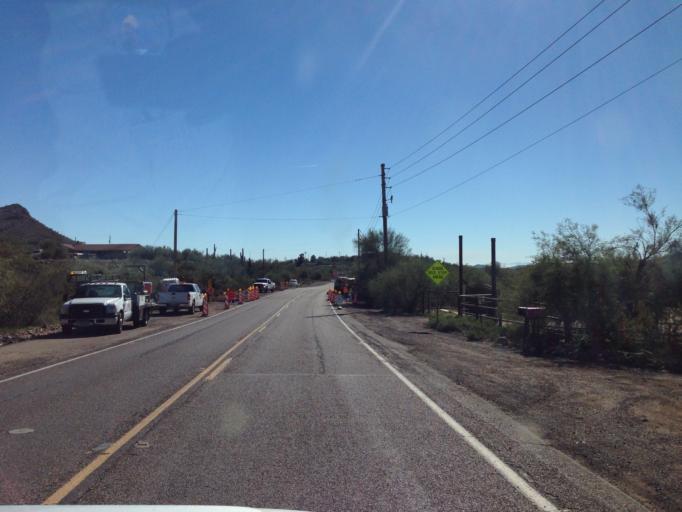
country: US
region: Arizona
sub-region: Maricopa County
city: New River
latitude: 33.8975
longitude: -112.0773
